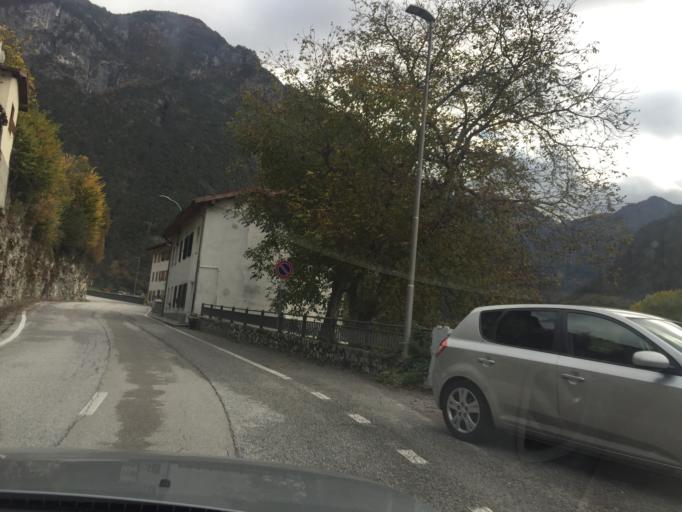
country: IT
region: Friuli Venezia Giulia
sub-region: Provincia di Udine
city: Chiusaforte
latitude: 46.4073
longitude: 13.3072
